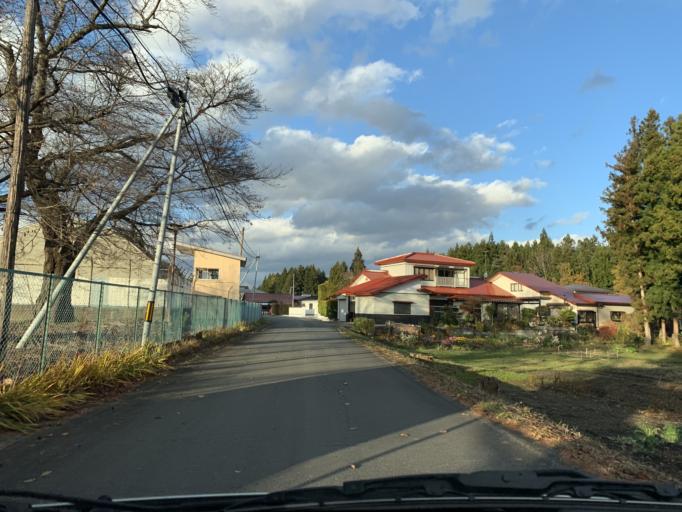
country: JP
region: Iwate
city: Mizusawa
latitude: 39.1275
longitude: 141.0309
